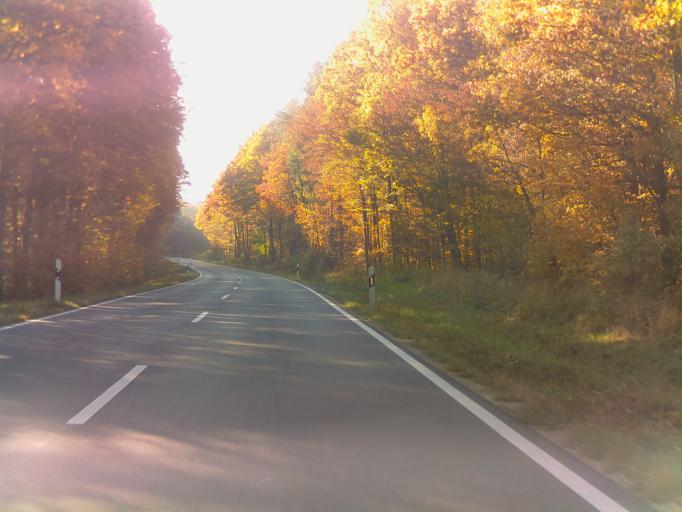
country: DE
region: Bavaria
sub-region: Regierungsbezirk Unterfranken
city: Eltmann
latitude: 49.9566
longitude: 10.6354
